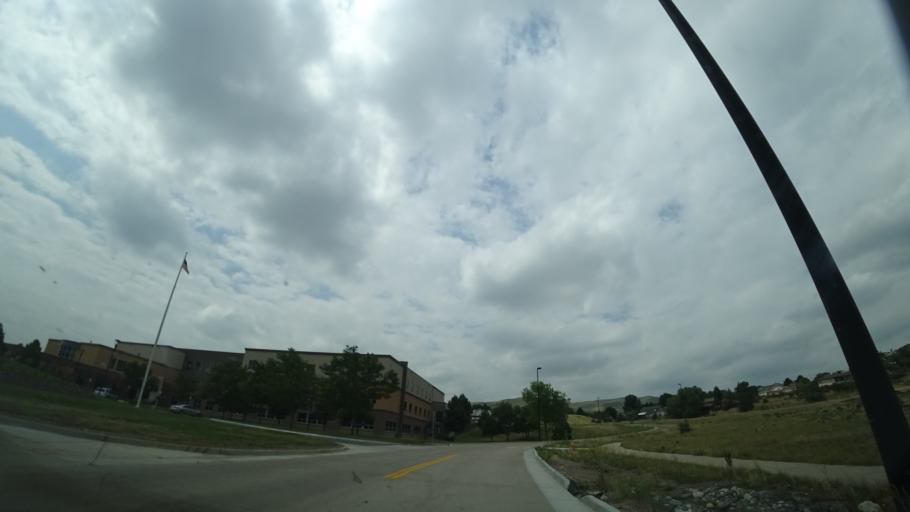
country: US
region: Colorado
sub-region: Jefferson County
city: West Pleasant View
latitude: 39.7160
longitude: -105.1516
